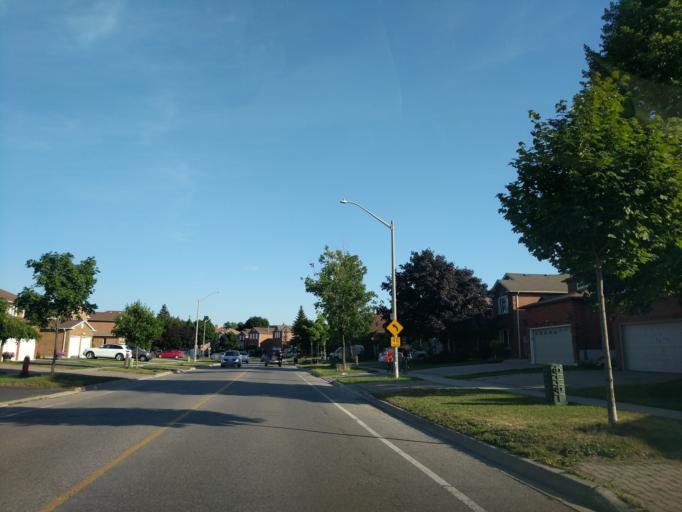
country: CA
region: Ontario
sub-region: York
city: Richmond Hill
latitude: 43.8466
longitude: -79.3996
